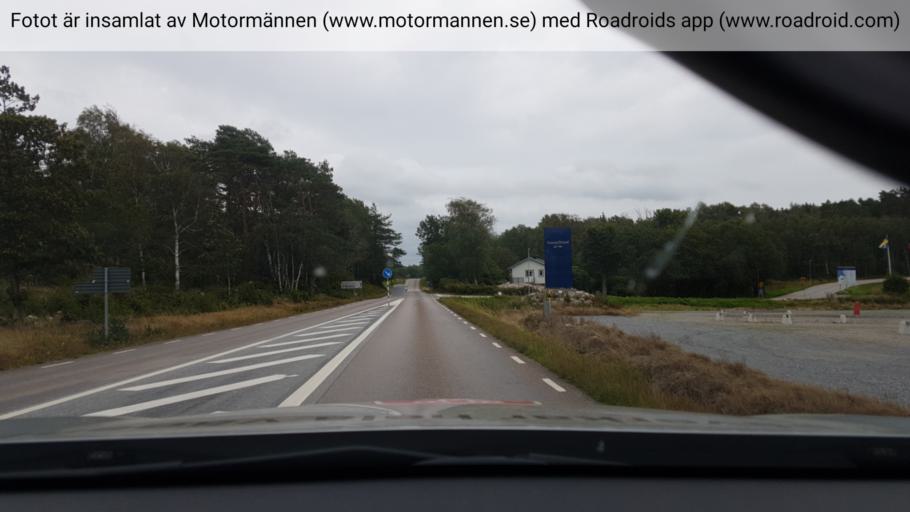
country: SE
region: Vaestra Goetaland
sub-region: Tanums Kommun
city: Grebbestad
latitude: 58.6778
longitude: 11.2773
